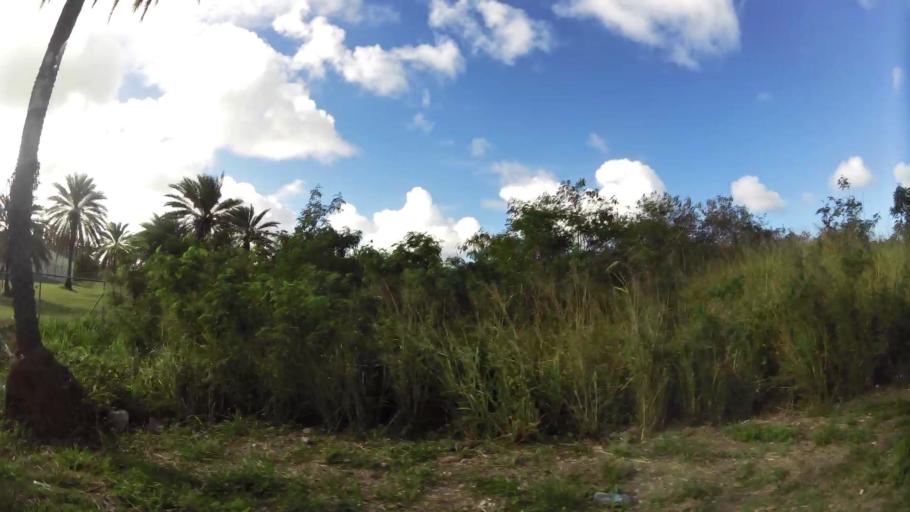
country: AG
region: Saint Peter
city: All Saints
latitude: 17.0711
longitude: -61.7889
